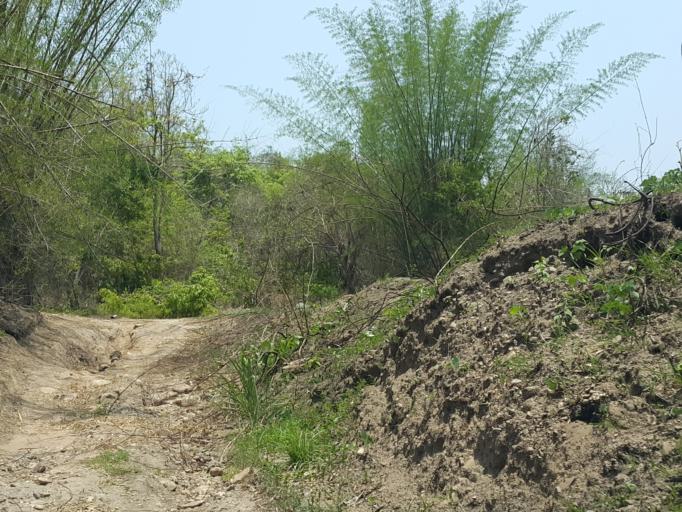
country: TH
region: Kanchanaburi
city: Sai Yok
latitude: 14.2264
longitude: 98.8826
